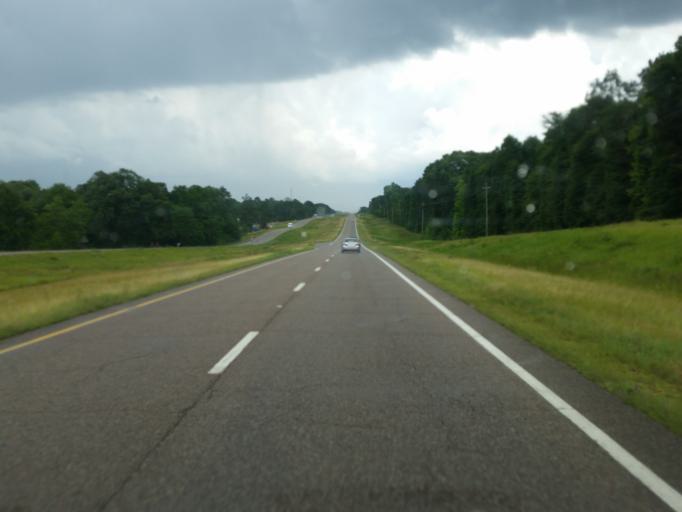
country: US
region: Mississippi
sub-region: George County
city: Lucedale
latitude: 30.9127
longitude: -88.4876
